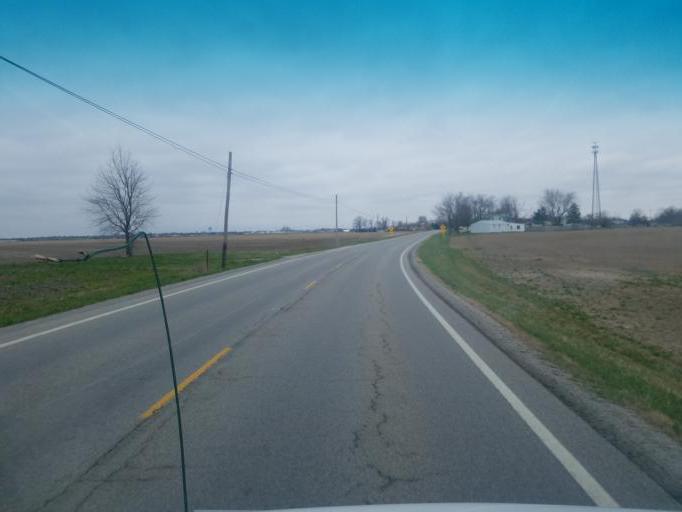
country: US
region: Ohio
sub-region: Van Wert County
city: Van Wert
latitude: 40.9036
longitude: -84.5670
